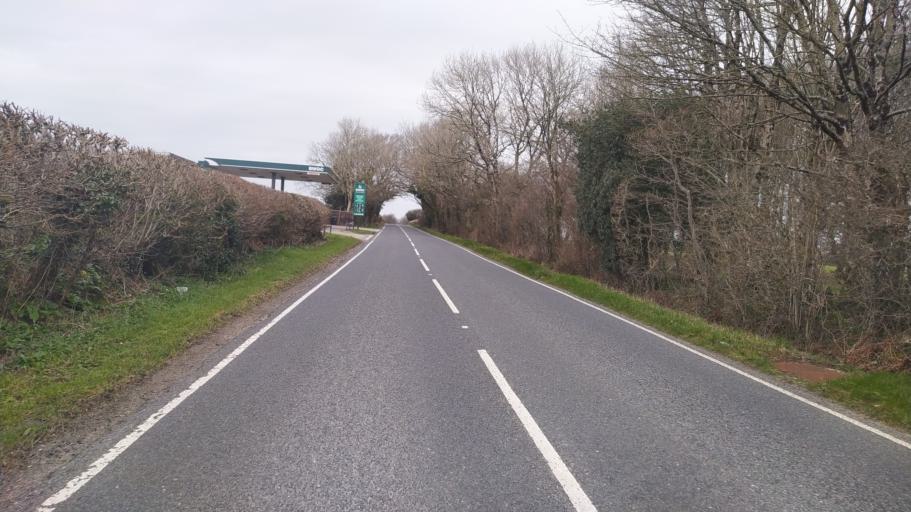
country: GB
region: England
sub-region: Dorset
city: Beaminster
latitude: 50.8146
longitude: -2.6540
